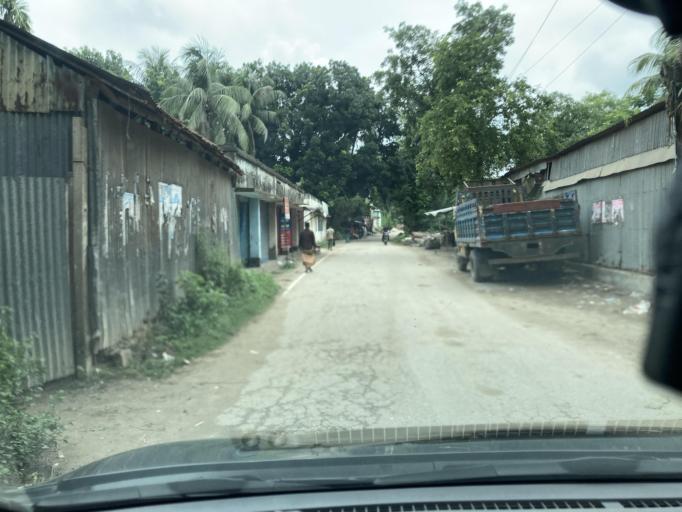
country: BD
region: Dhaka
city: Dohar
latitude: 23.7617
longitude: 90.1954
